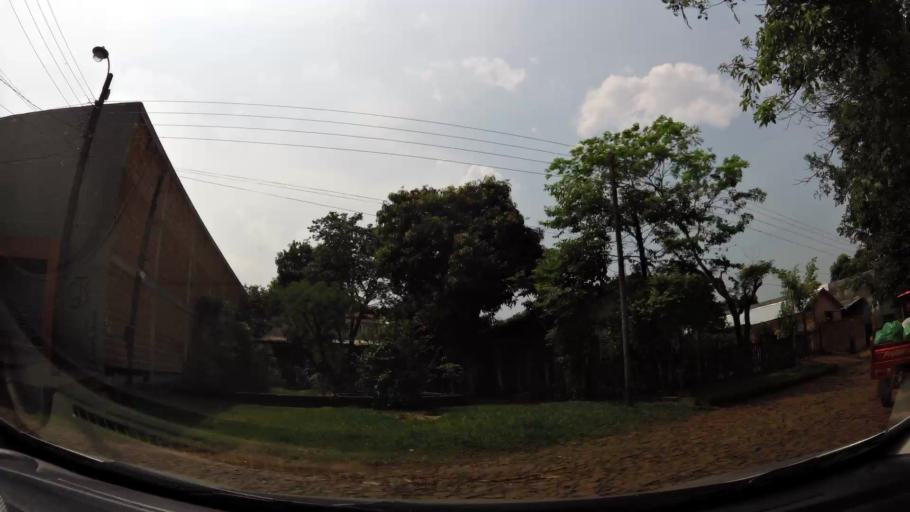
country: PY
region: Alto Parana
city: Presidente Franco
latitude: -25.5434
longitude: -54.6307
